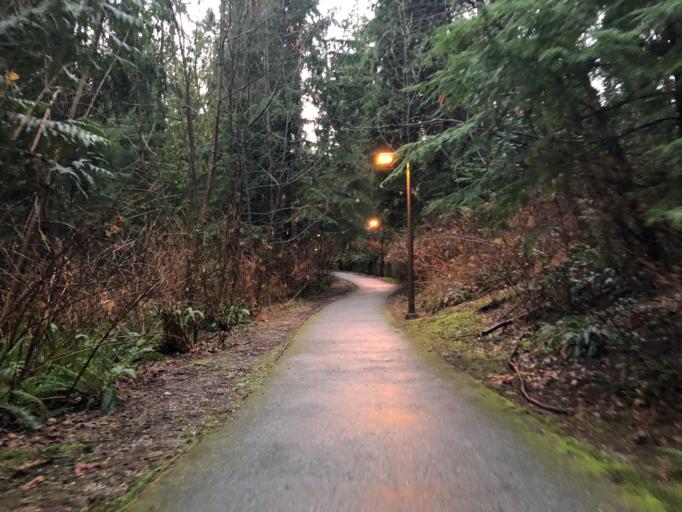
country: CA
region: British Columbia
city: Burnaby
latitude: 49.3228
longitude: -122.9541
